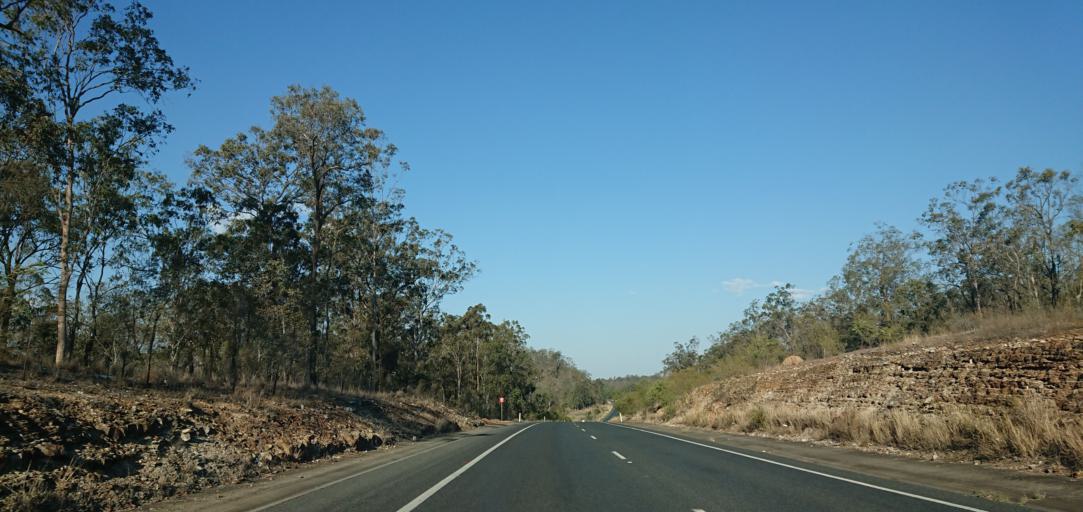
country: AU
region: Queensland
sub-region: Lockyer Valley
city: Gatton
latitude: -27.5525
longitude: 152.1697
